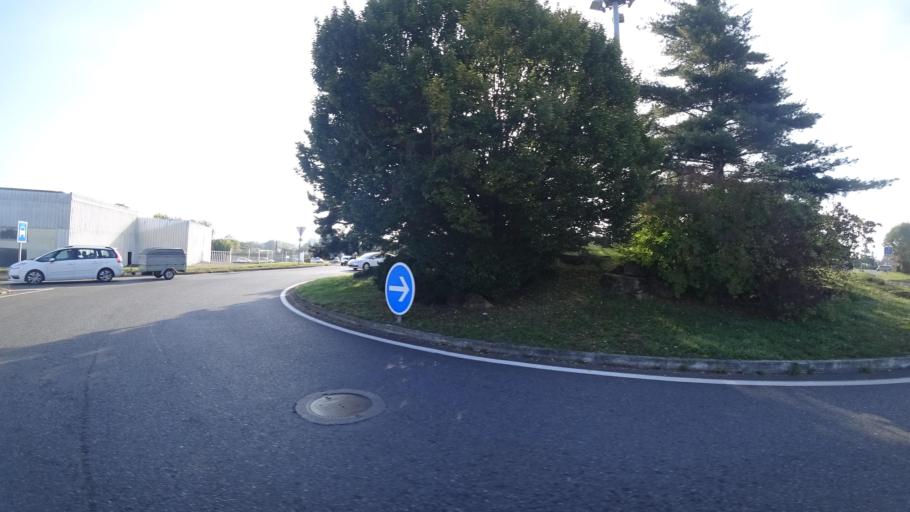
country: FR
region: Midi-Pyrenees
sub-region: Departement de l'Aveyron
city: Olemps
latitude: 44.3255
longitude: 2.5587
